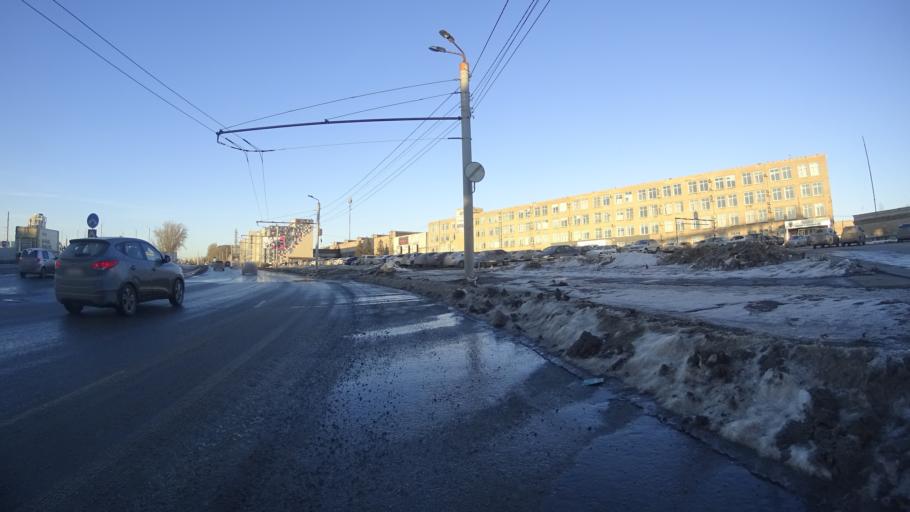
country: RU
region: Chelyabinsk
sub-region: Gorod Chelyabinsk
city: Chelyabinsk
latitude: 55.1539
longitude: 61.4439
